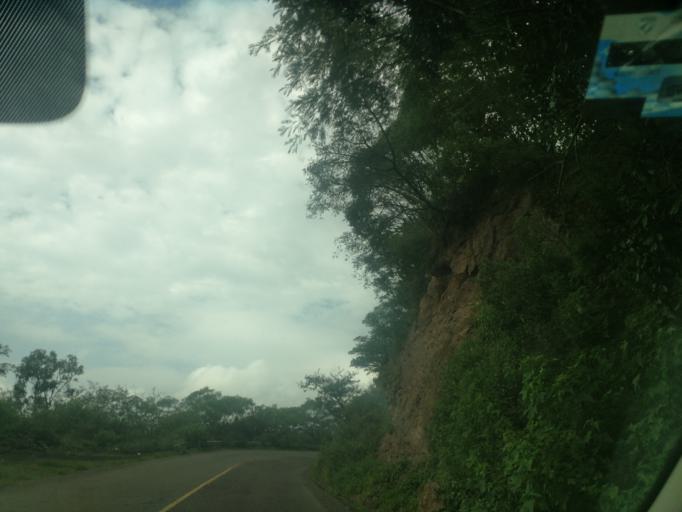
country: MX
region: Jalisco
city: El Salto
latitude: 20.3680
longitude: -104.5890
